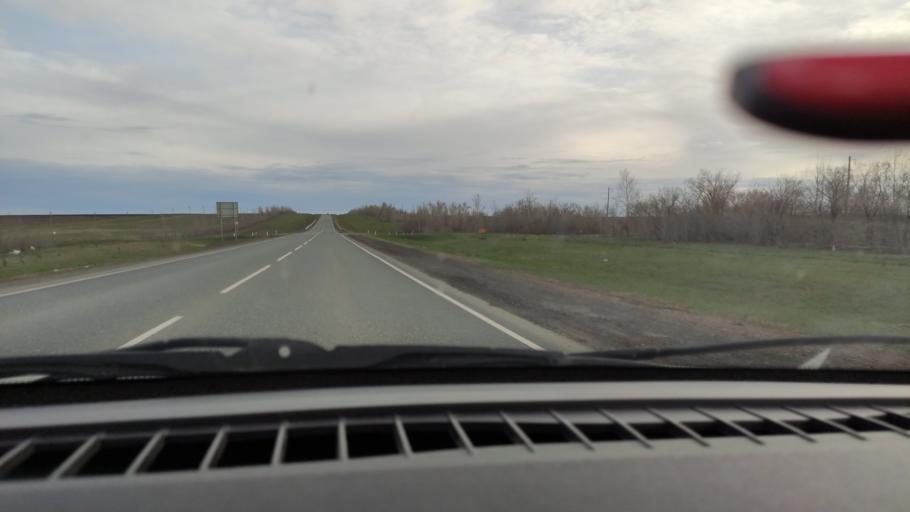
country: RU
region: Orenburg
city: Sakmara
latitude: 52.0772
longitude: 55.2648
